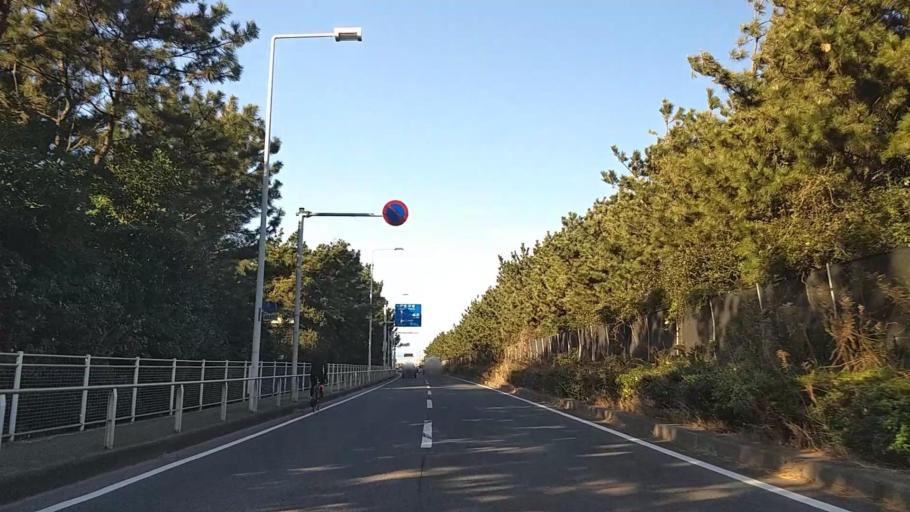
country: JP
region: Kanagawa
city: Chigasaki
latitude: 35.3205
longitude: 139.4401
